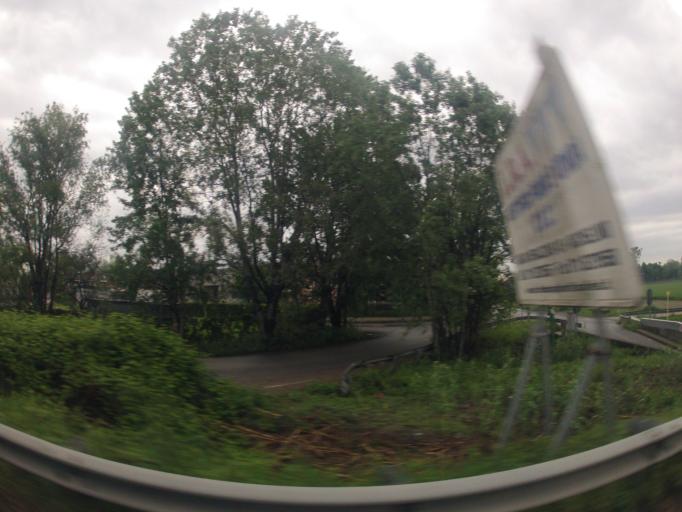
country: IT
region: Piedmont
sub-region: Provincia di Torino
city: La Loggia
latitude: 44.9647
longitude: 7.6761
